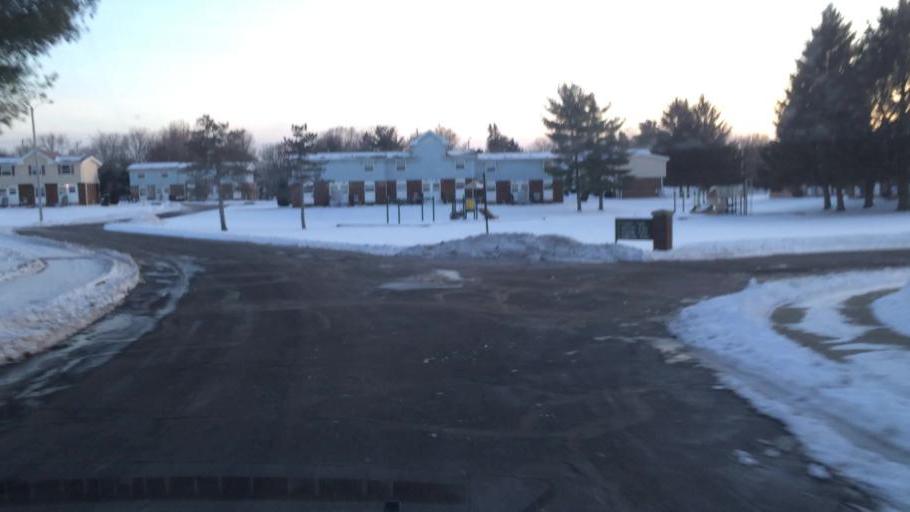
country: US
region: Ohio
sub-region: Summit County
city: Barberton
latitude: 41.0044
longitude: -81.5993
